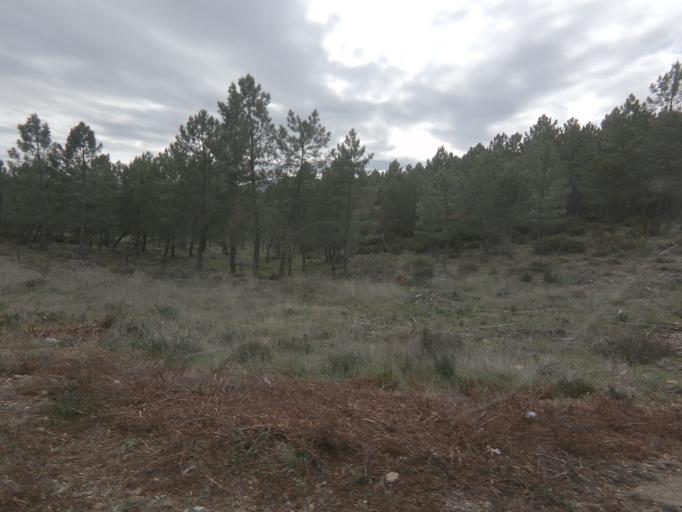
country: ES
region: Castille and Leon
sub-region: Provincia de Salamanca
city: Penaparda
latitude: 40.2612
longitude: -6.6891
